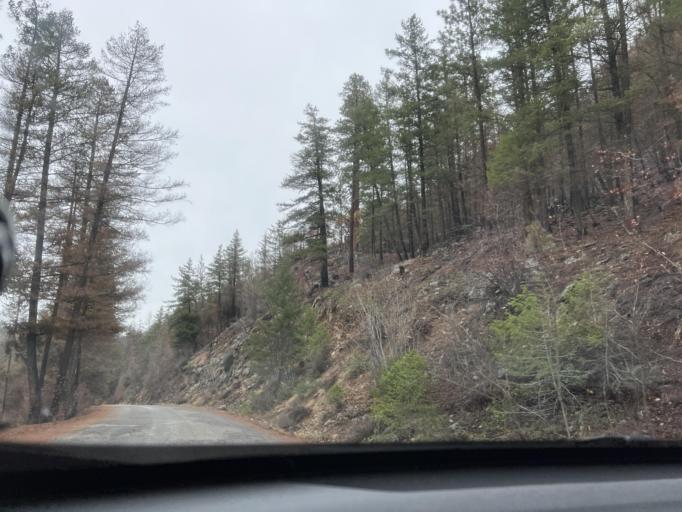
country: US
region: Washington
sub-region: Okanogan County
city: Brewster
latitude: 48.5668
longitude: -120.1750
